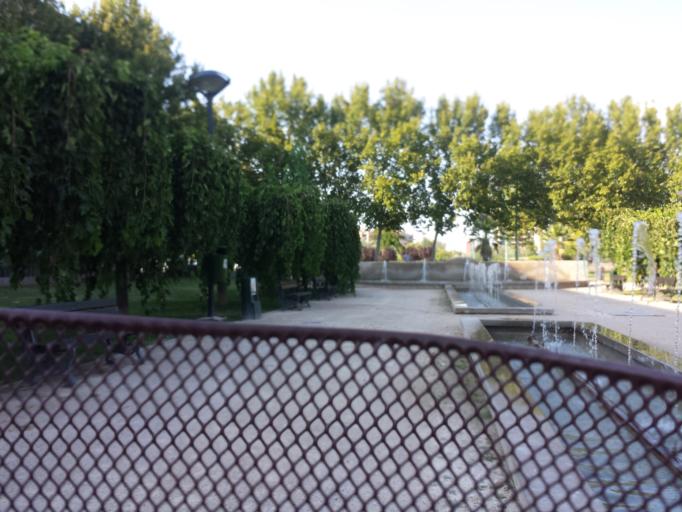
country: ES
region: Aragon
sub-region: Provincia de Zaragoza
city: Zaragoza
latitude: 41.6518
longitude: -0.8660
